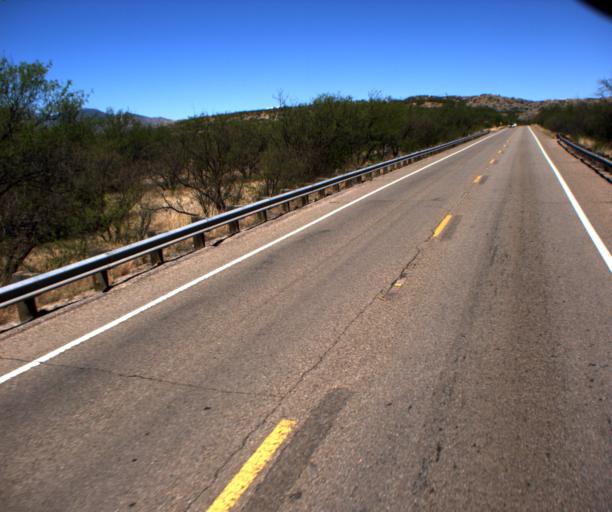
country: US
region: Arizona
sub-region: Santa Cruz County
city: Rio Rico
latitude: 31.6422
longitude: -110.7144
